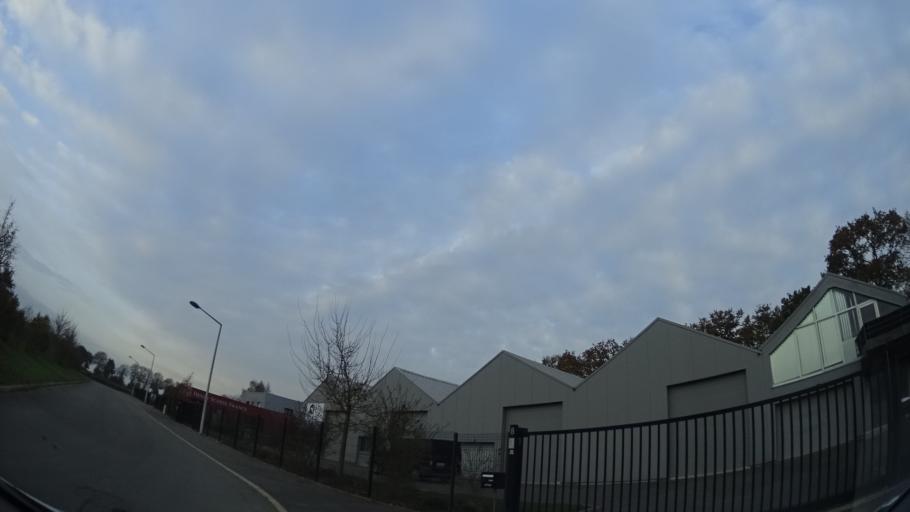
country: FR
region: Brittany
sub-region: Departement d'Ille-et-Vilaine
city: La Chapelle-des-Fougeretz
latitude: 48.1919
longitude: -1.7330
